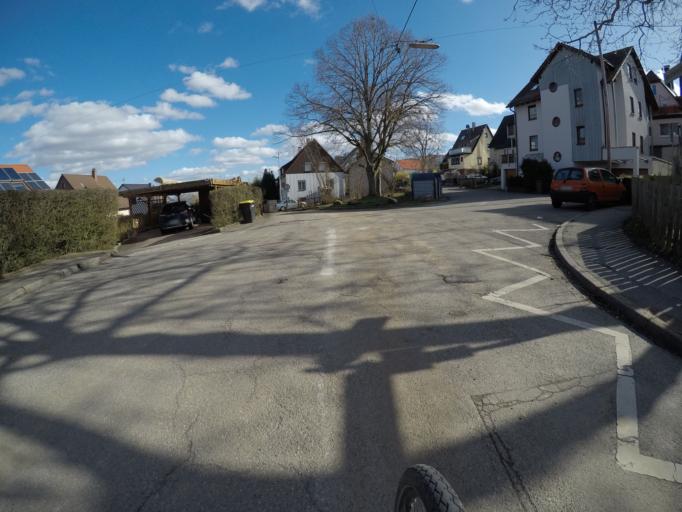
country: DE
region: Baden-Wuerttemberg
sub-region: Regierungsbezirk Stuttgart
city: Filderstadt
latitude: 48.6595
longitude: 9.1869
